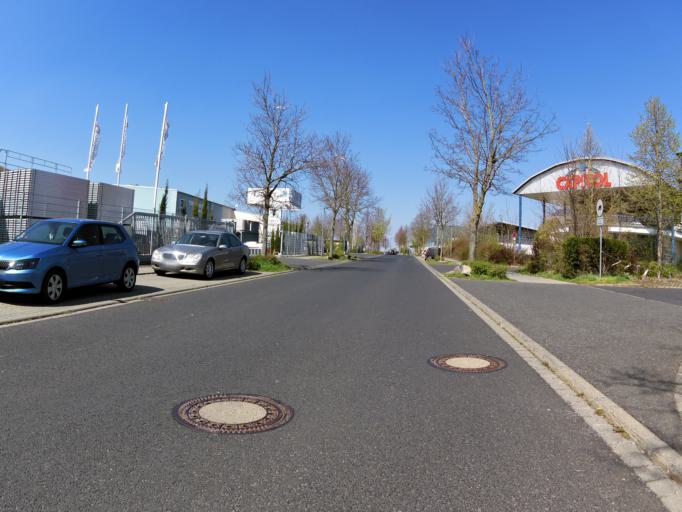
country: DE
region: Bavaria
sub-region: Regierungsbezirk Unterfranken
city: Biebelried
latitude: 49.7796
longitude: 10.0696
